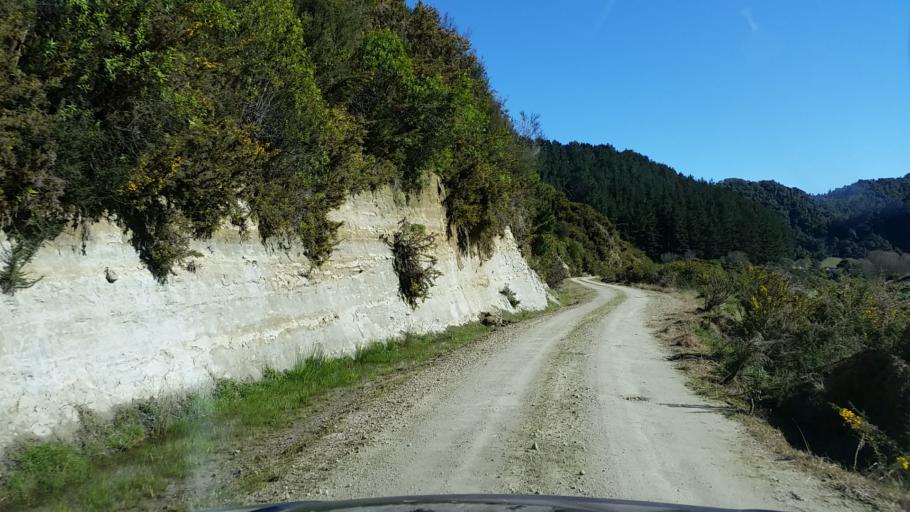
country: NZ
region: Manawatu-Wanganui
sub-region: Wanganui District
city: Wanganui
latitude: -39.6680
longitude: 174.8706
